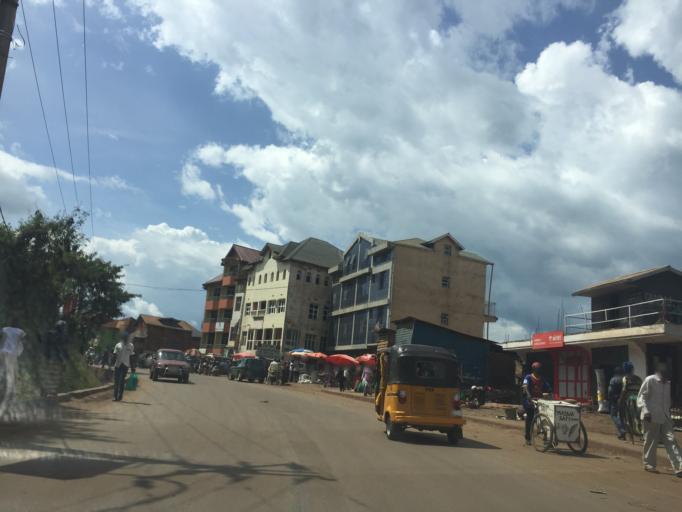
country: CD
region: South Kivu
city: Bukavu
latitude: -2.4952
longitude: 28.8506
